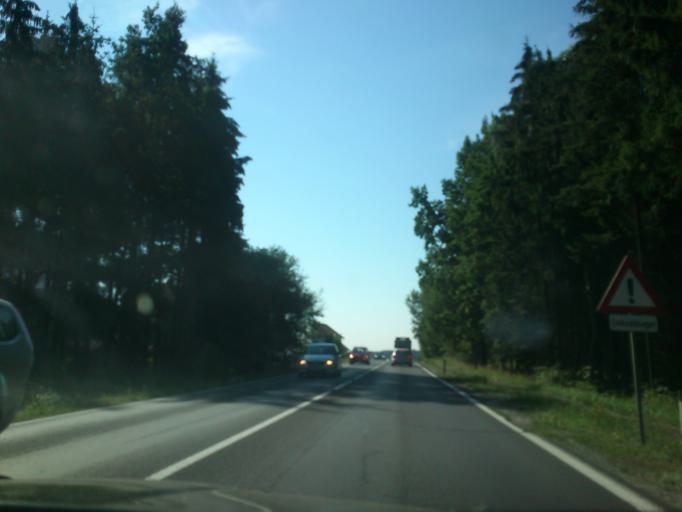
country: AT
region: Upper Austria
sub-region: Politischer Bezirk Freistadt
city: Freistadt
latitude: 48.4787
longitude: 14.4981
